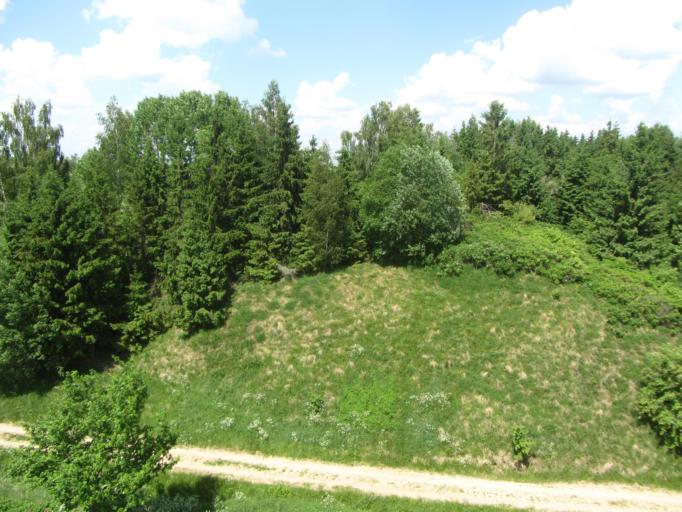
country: LT
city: Jieznas
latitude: 54.6596
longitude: 24.2236
